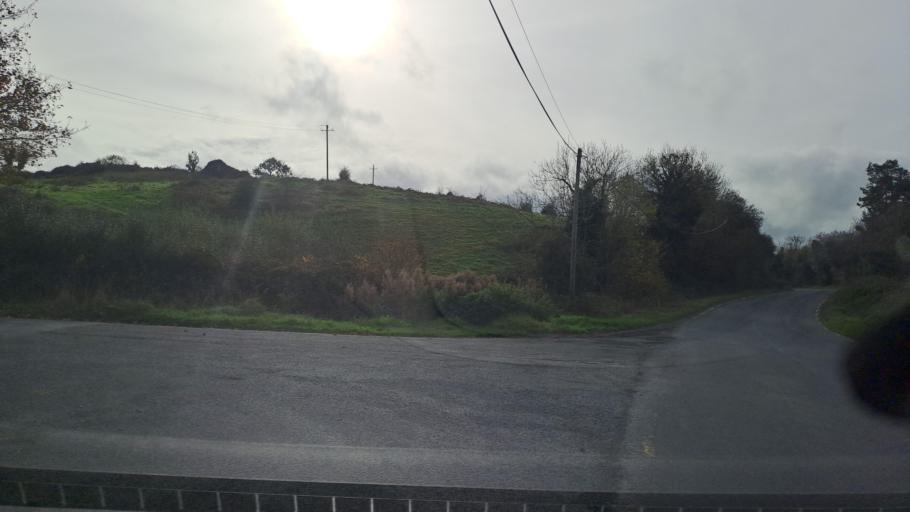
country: IE
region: Ulster
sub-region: An Cabhan
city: Bailieborough
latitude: 54.0228
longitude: -6.9315
